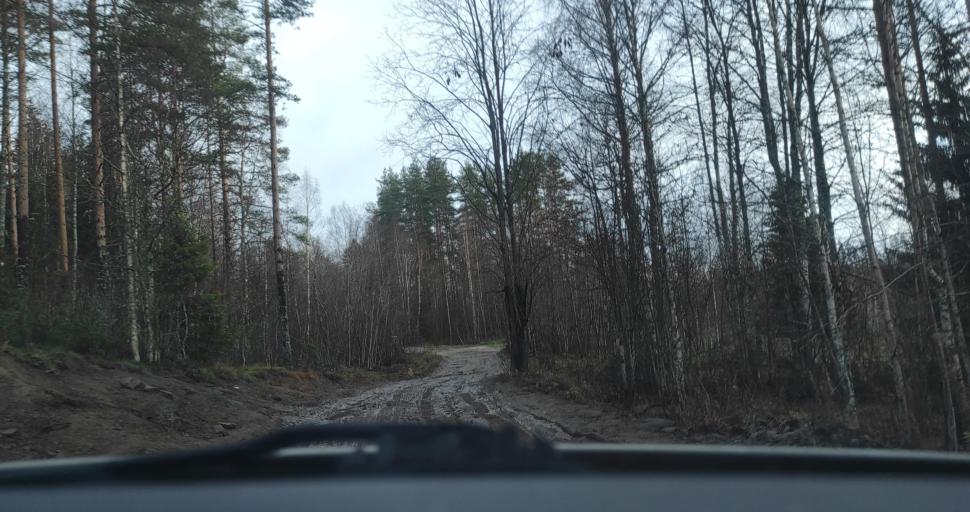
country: RU
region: Republic of Karelia
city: Pitkyaranta
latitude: 61.7421
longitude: 31.3924
